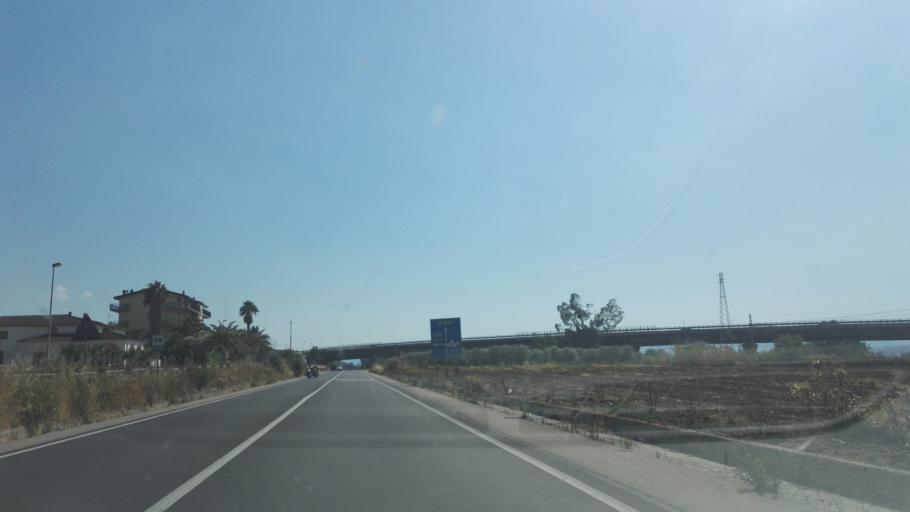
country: IT
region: Calabria
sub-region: Provincia di Cosenza
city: Tarsia
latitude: 39.6377
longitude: 16.2342
